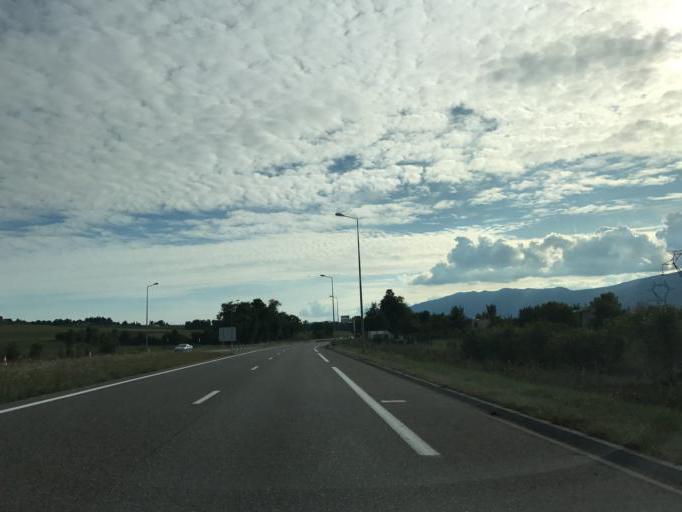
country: FR
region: Rhone-Alpes
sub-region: Departement de l'Ain
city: Saint-Genis-Pouilly
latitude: 46.2380
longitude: 6.0313
